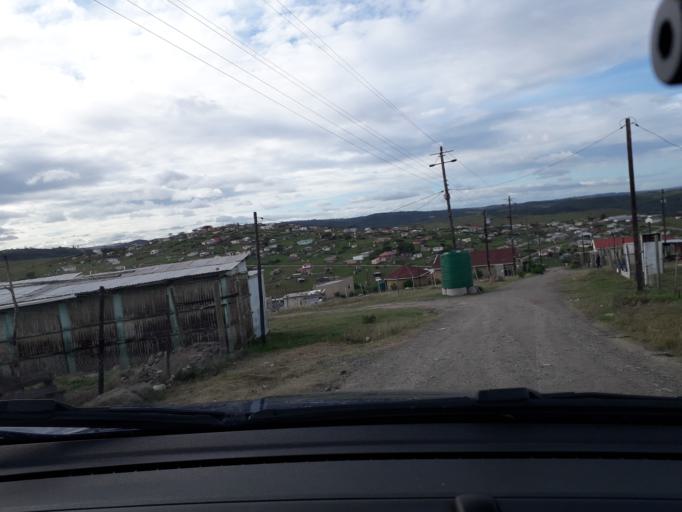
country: ZA
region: Eastern Cape
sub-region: Buffalo City Metropolitan Municipality
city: East London
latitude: -32.8512
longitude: 27.9838
